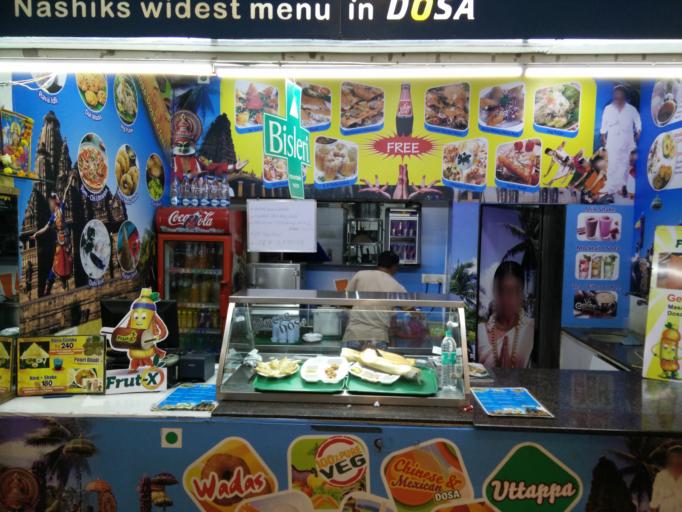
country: IN
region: Maharashtra
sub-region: Nashik Division
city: Nashik
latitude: 19.9906
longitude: 73.7634
